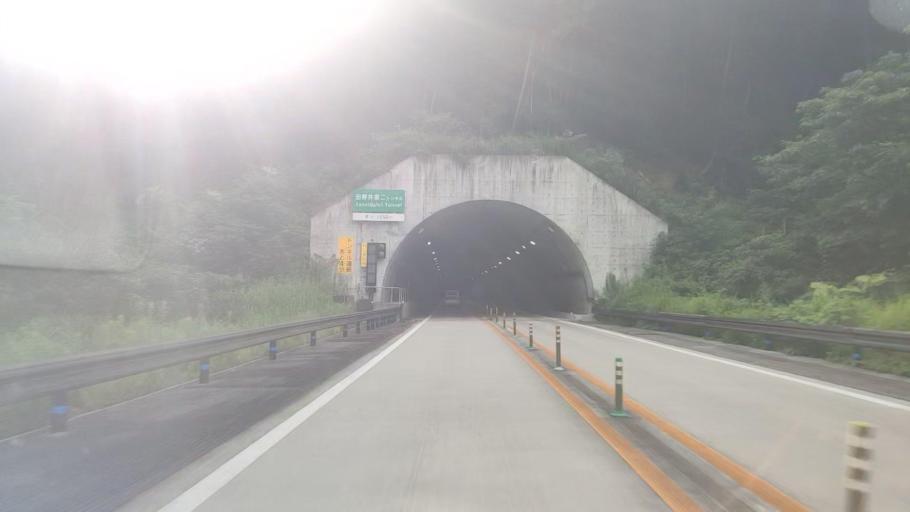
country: JP
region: Wakayama
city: Tanabe
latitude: 33.5862
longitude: 135.4466
